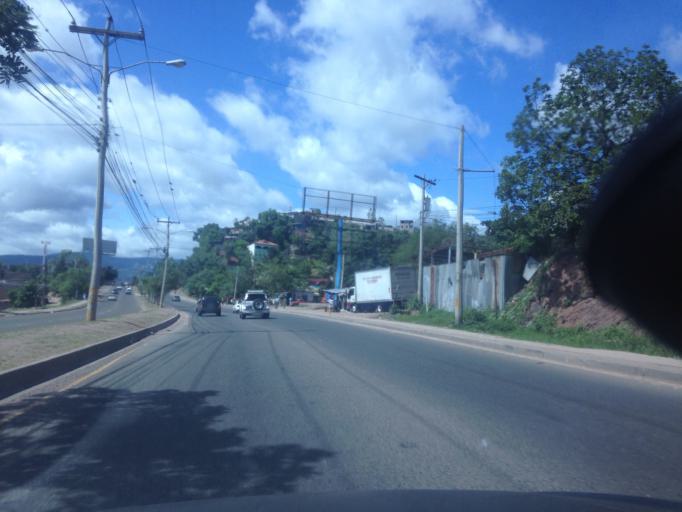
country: HN
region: Francisco Morazan
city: El Tablon
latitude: 14.0608
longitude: -87.1743
